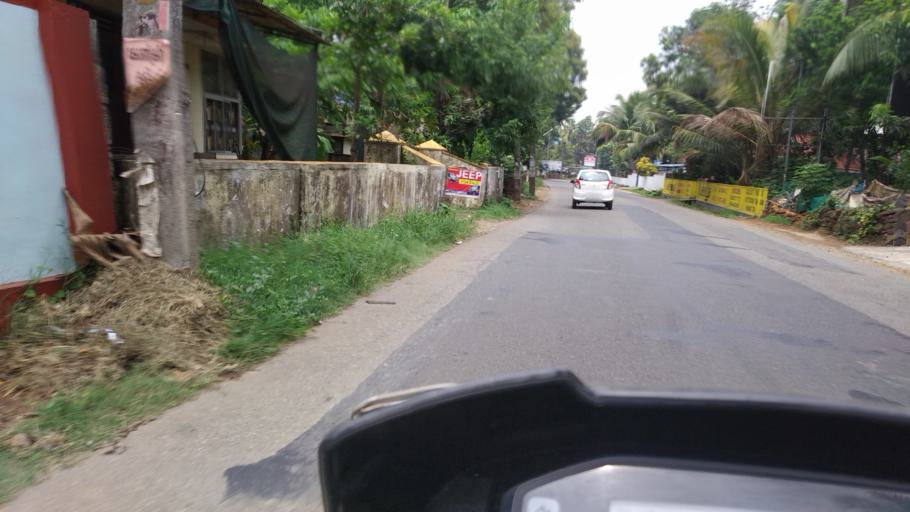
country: IN
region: Kerala
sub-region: Ernakulam
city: Perumpavur
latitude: 10.1105
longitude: 76.5334
